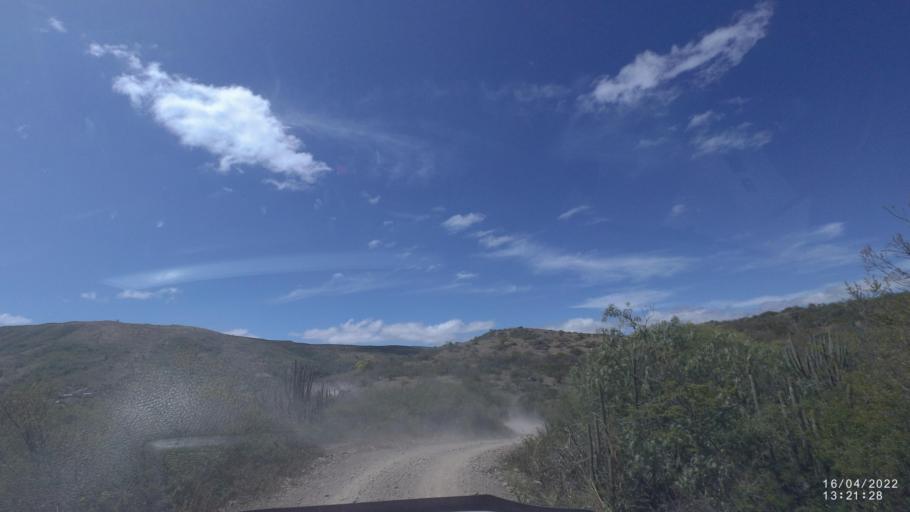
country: BO
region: Cochabamba
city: Mizque
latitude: -17.9923
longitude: -65.6106
